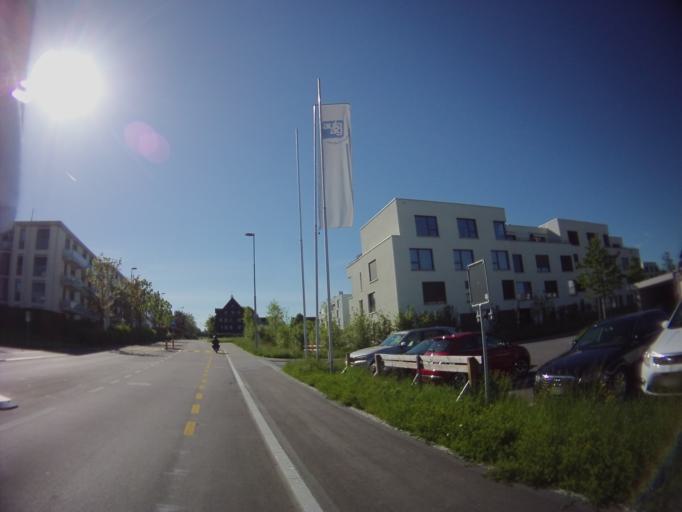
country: CH
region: Zug
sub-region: Zug
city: Cham
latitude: 47.1798
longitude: 8.4496
